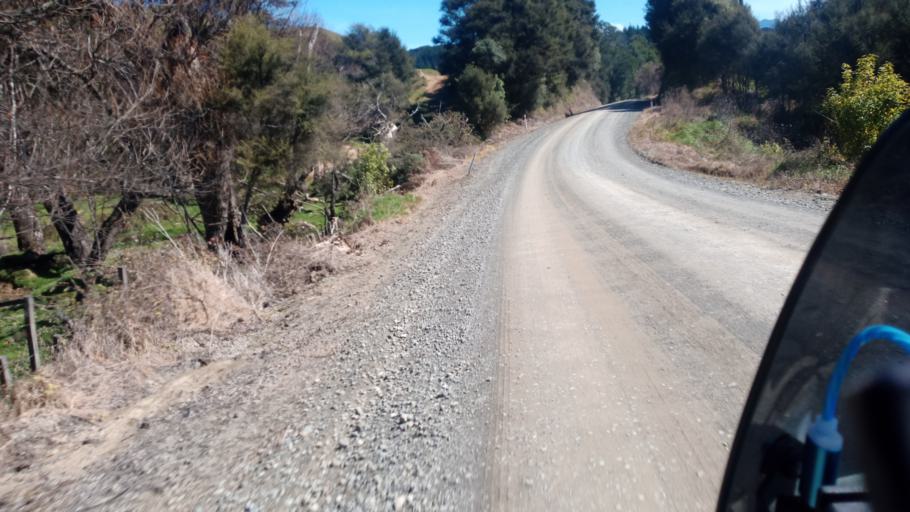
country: NZ
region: Gisborne
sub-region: Gisborne District
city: Gisborne
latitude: -37.9889
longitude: 178.2843
